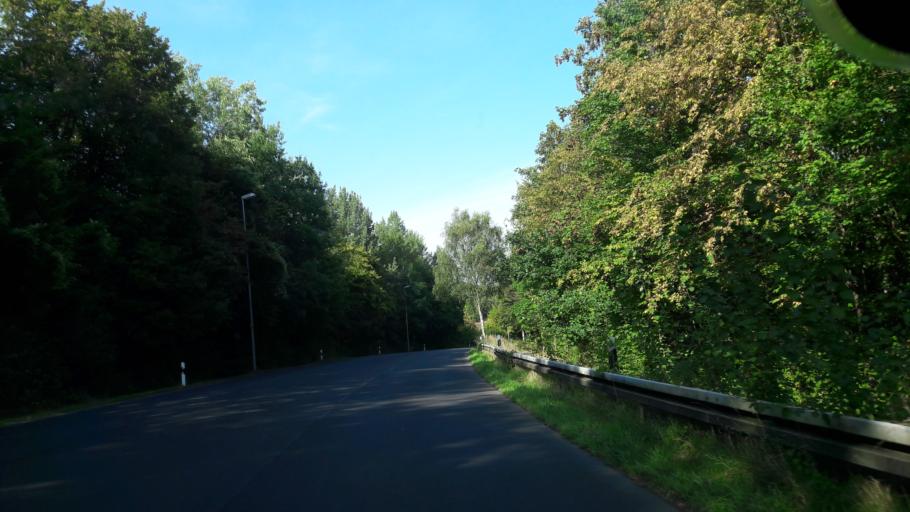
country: DE
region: Lower Saxony
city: Diekholzen
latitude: 52.1230
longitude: 9.9036
